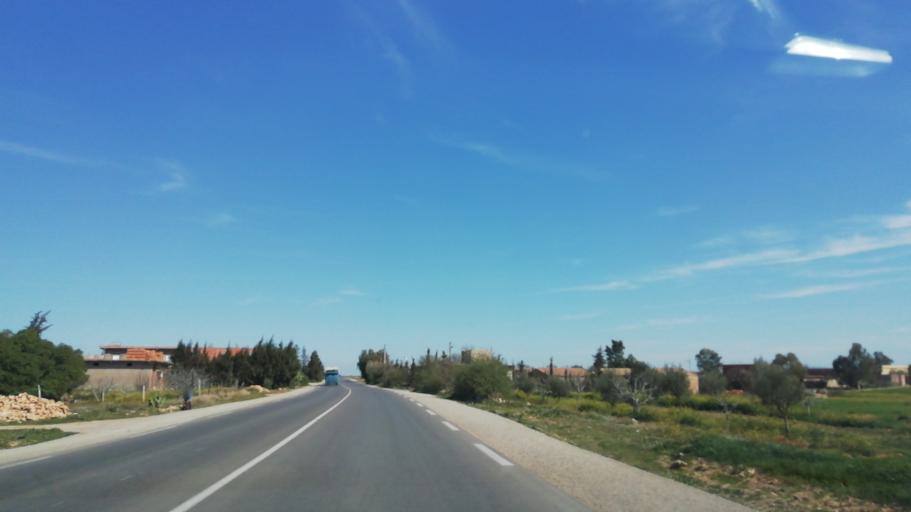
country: DZ
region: Mascara
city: Mascara
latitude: 35.4148
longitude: 0.3910
